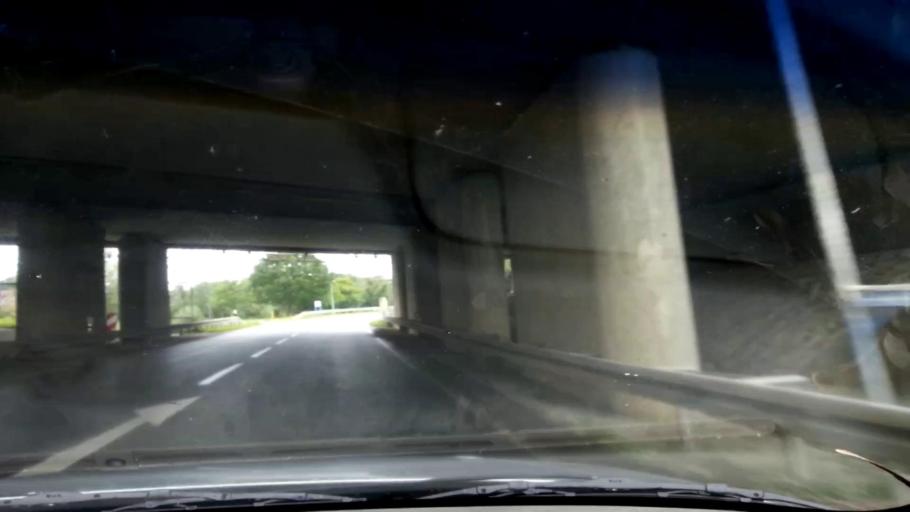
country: DE
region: Bavaria
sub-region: Upper Franconia
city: Memmelsdorf
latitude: 49.9374
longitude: 10.9545
